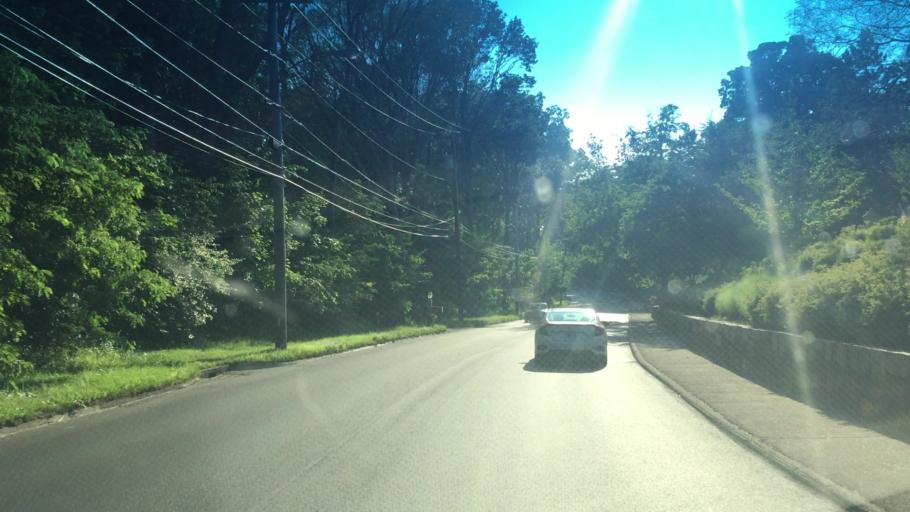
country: US
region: Massachusetts
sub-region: Norfolk County
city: Medfield
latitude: 42.1833
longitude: -71.3090
